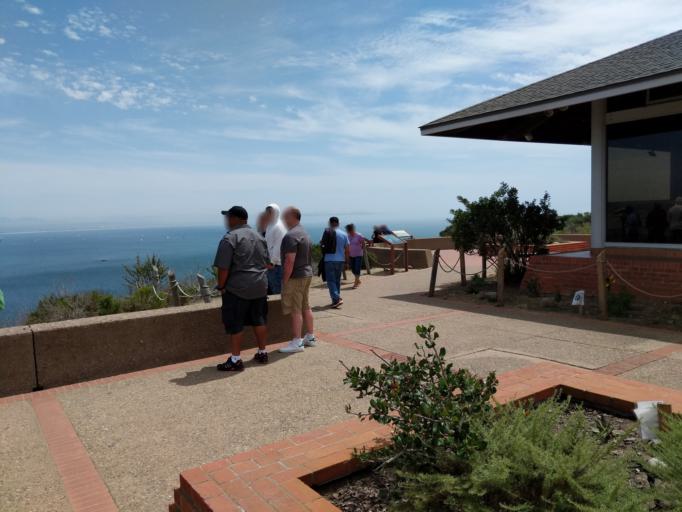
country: US
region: California
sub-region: San Diego County
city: Coronado
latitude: 32.6750
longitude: -117.2393
